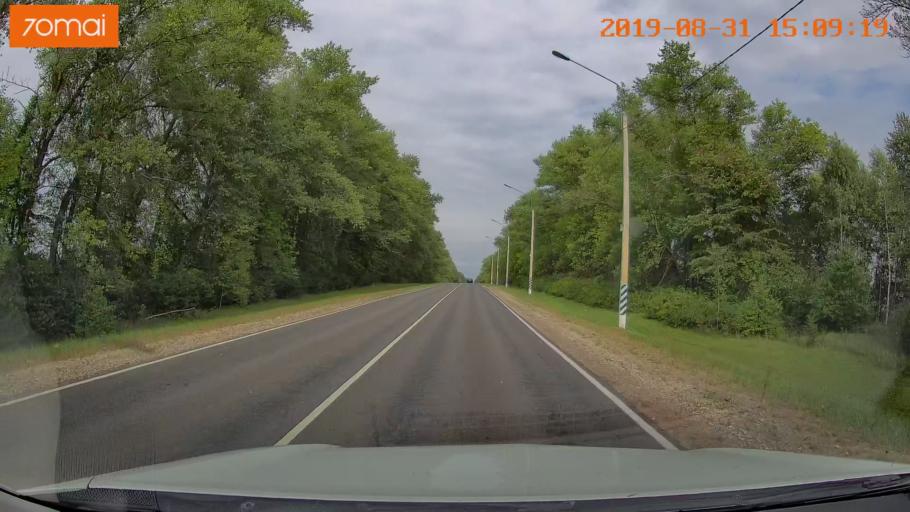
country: RU
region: Kaluga
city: Spas-Demensk
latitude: 54.4004
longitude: 34.1984
